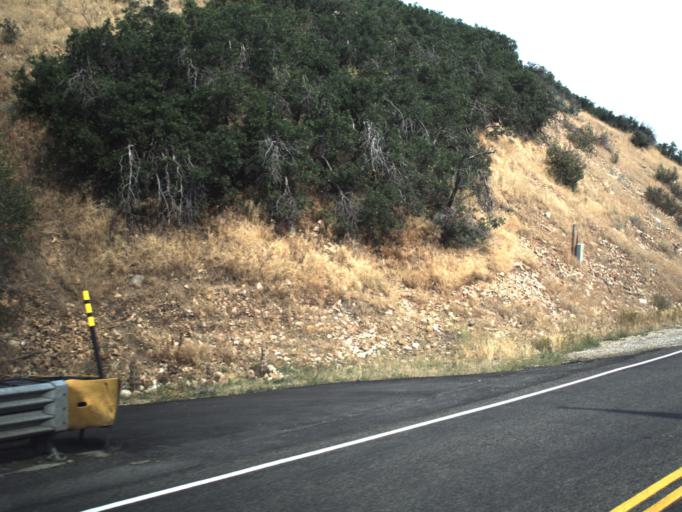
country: US
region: Utah
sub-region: Summit County
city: Kamas
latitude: 40.6426
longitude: -111.2721
